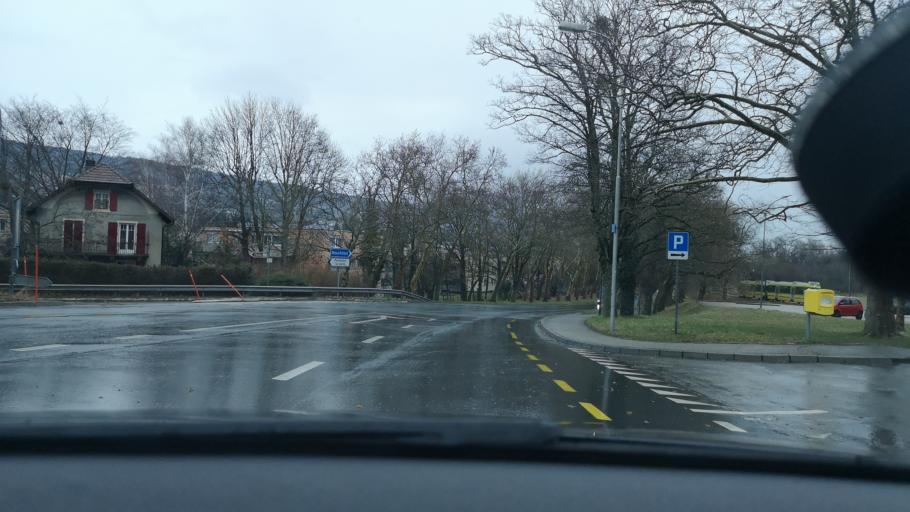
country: CH
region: Neuchatel
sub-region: Boudry District
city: Auvernier
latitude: 46.9663
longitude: 6.8647
